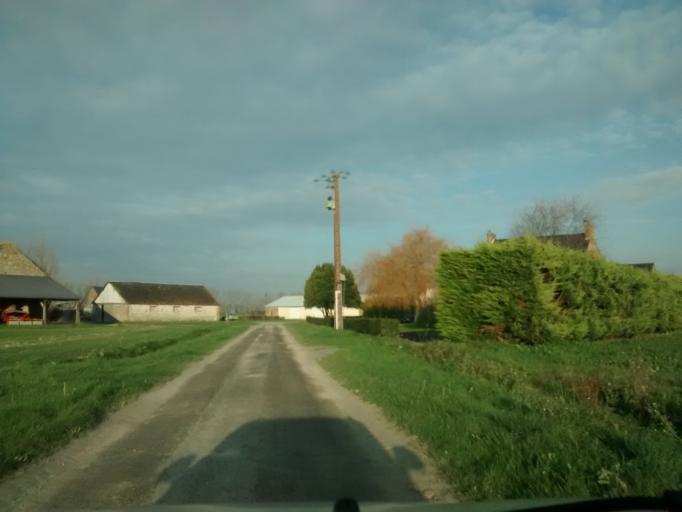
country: FR
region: Brittany
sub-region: Departement d'Ille-et-Vilaine
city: Roz-sur-Couesnon
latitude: 48.6055
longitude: -1.5863
